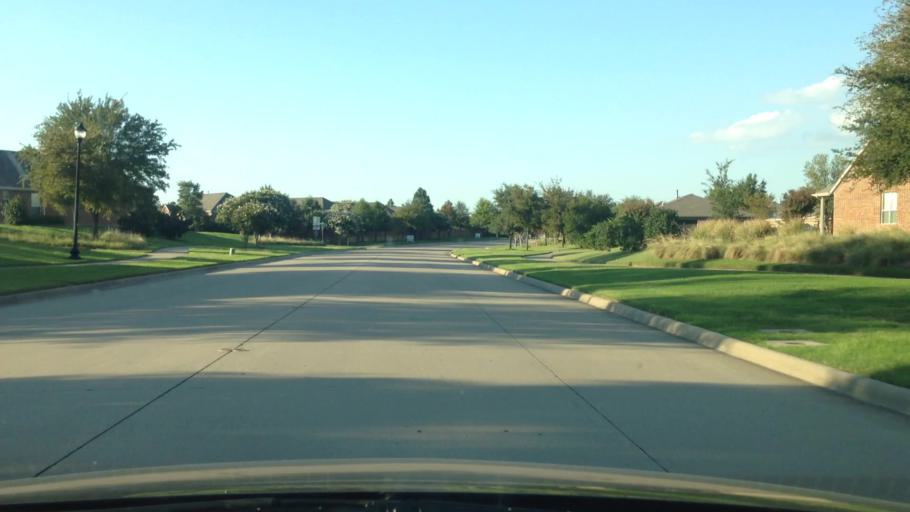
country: US
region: Texas
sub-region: Denton County
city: Little Elm
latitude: 33.1425
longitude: -96.8968
